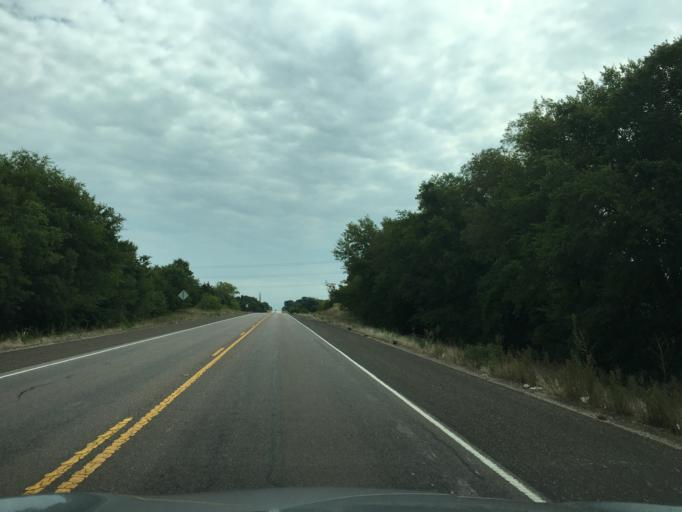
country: US
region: Texas
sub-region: Collin County
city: Anna
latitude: 33.3182
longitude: -96.5037
